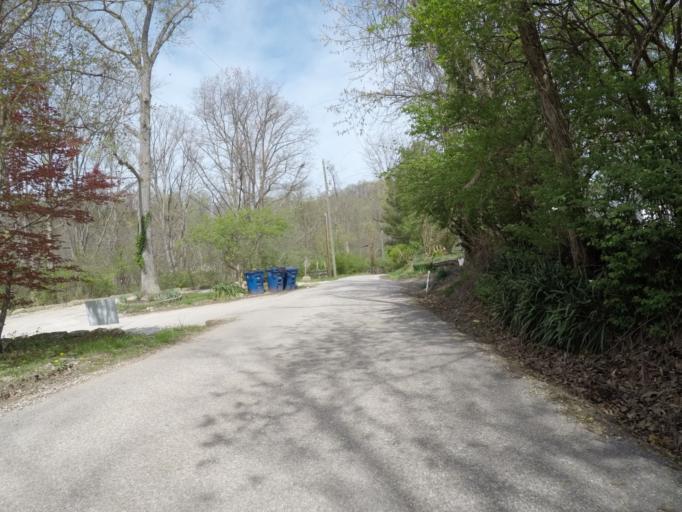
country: US
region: West Virginia
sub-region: Wayne County
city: Lavalette
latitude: 38.3437
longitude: -82.3744
